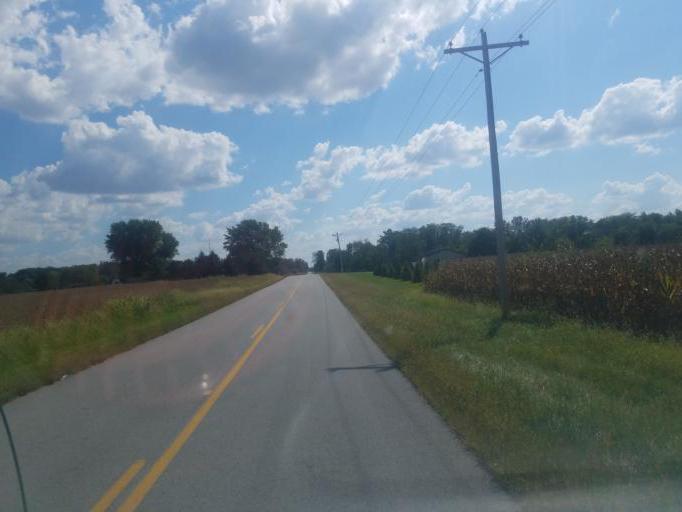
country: US
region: Ohio
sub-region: Auglaize County
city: Saint Marys
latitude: 40.6012
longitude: -84.3392
